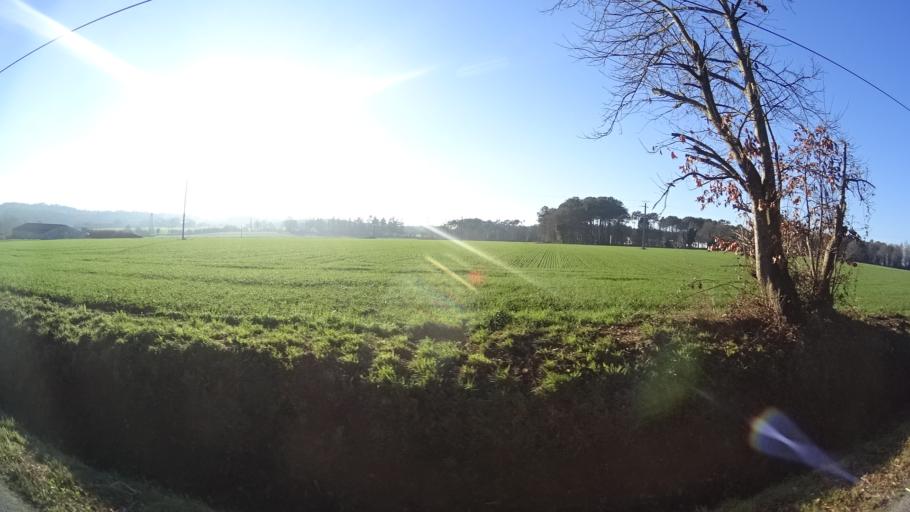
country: FR
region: Brittany
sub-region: Departement du Morbihan
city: Saint-Vincent-sur-Oust
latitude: 47.6777
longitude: -2.1759
